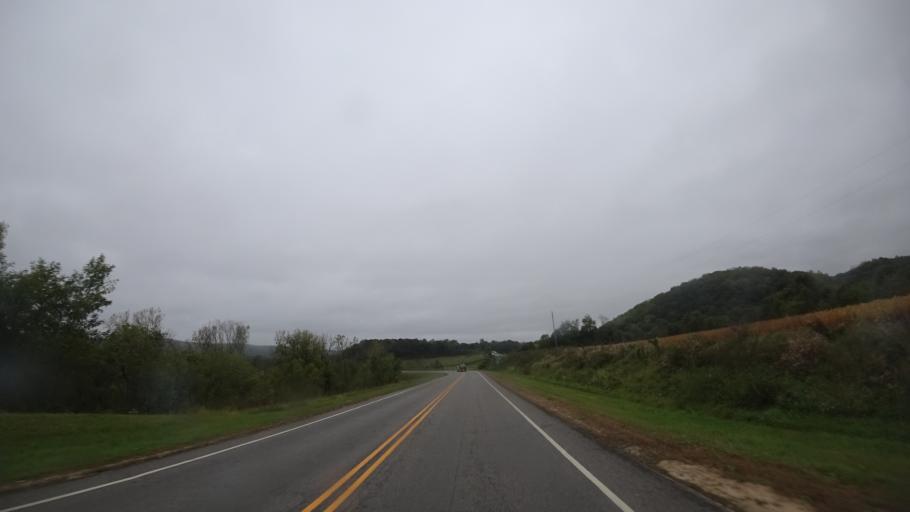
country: US
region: Wisconsin
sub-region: Crawford County
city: Prairie du Chien
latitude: 43.0466
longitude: -90.9858
